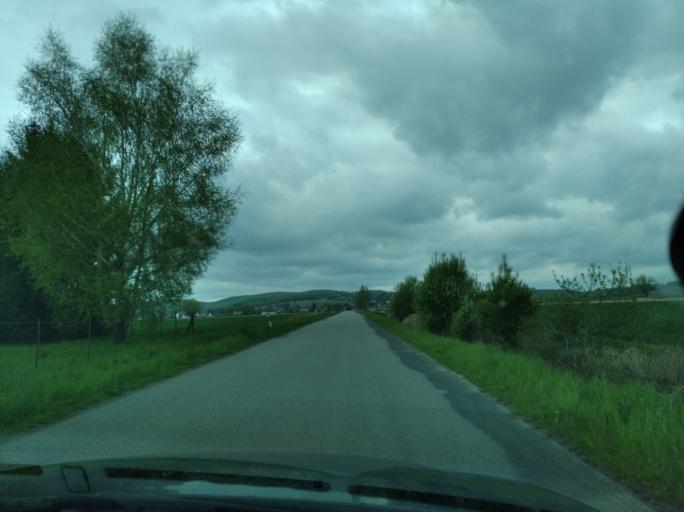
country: PL
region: Subcarpathian Voivodeship
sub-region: Powiat sanocki
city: Dlugie
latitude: 49.5943
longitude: 22.0495
